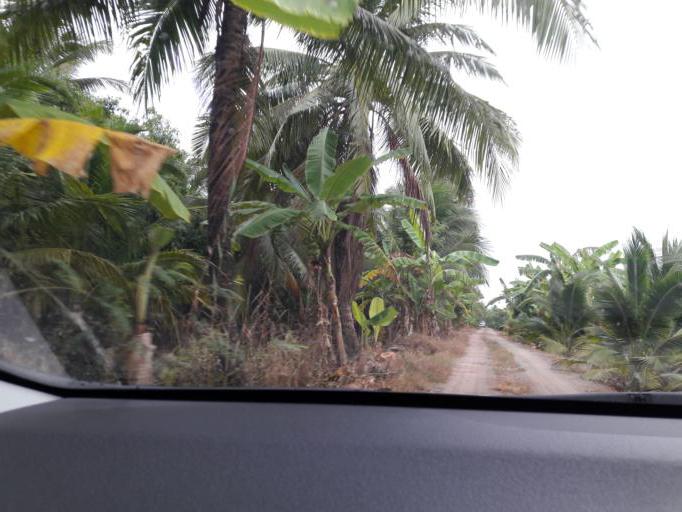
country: TH
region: Ratchaburi
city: Damnoen Saduak
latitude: 13.5748
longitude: 100.0195
